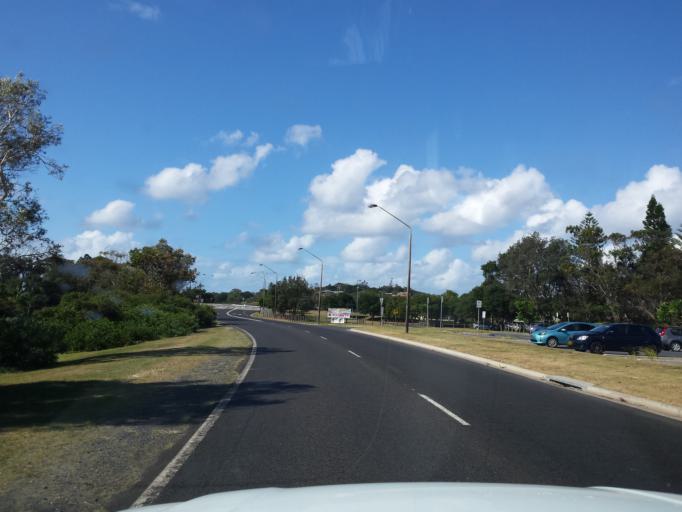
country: AU
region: New South Wales
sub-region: Ballina
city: East Ballina
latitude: -28.8711
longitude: 153.5737
